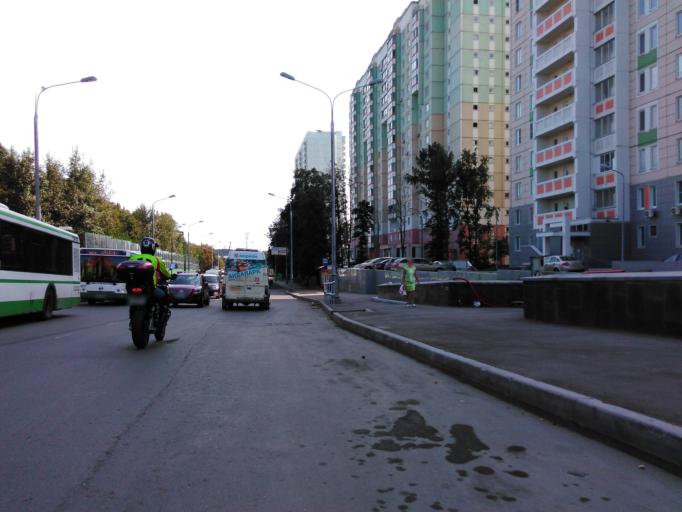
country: RU
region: Moskovskaya
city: Bol'shaya Setun'
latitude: 55.7139
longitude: 37.4033
